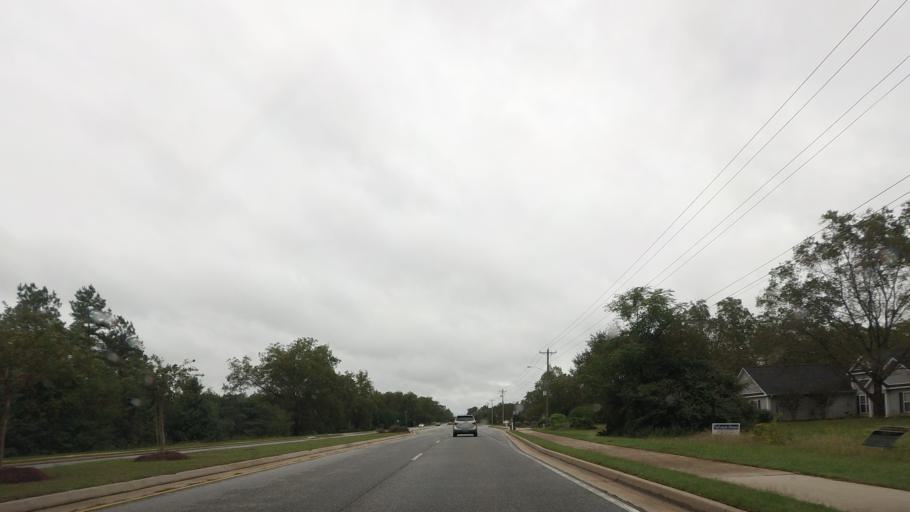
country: US
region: Georgia
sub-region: Houston County
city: Perry
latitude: 32.5162
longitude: -83.6624
